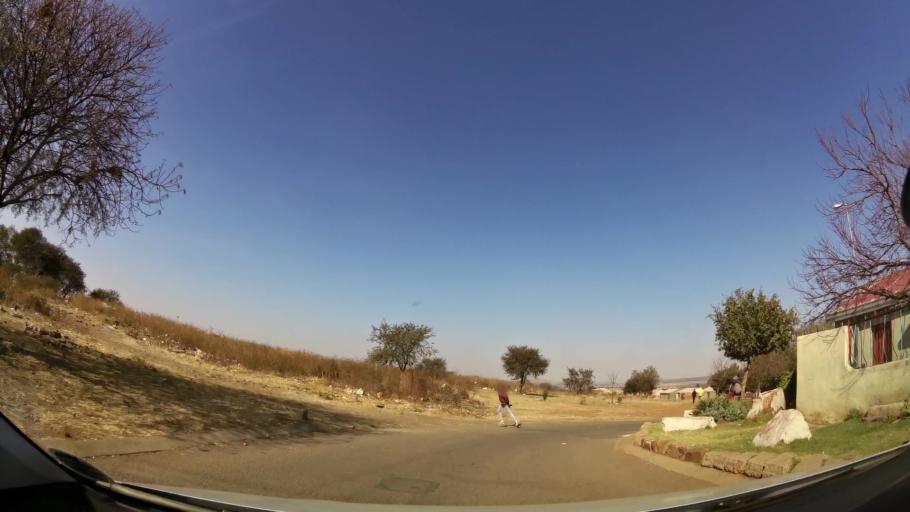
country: ZA
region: Gauteng
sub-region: City of Johannesburg Metropolitan Municipality
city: Soweto
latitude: -26.2831
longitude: 27.8712
